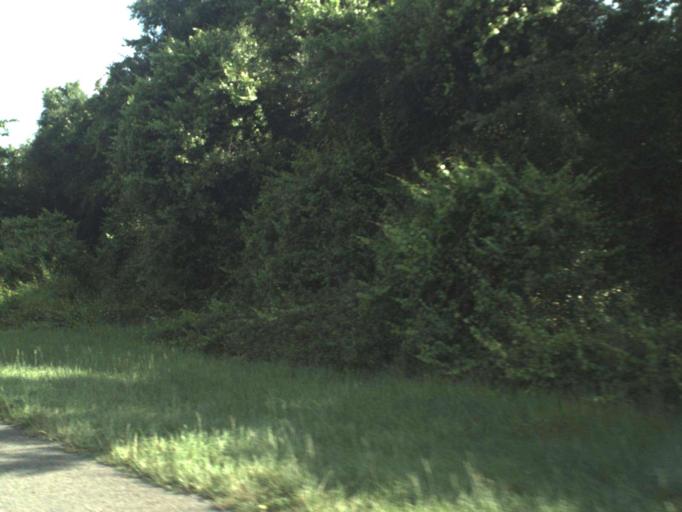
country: US
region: Florida
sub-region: Lake County
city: Groveland
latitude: 28.5156
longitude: -81.8424
